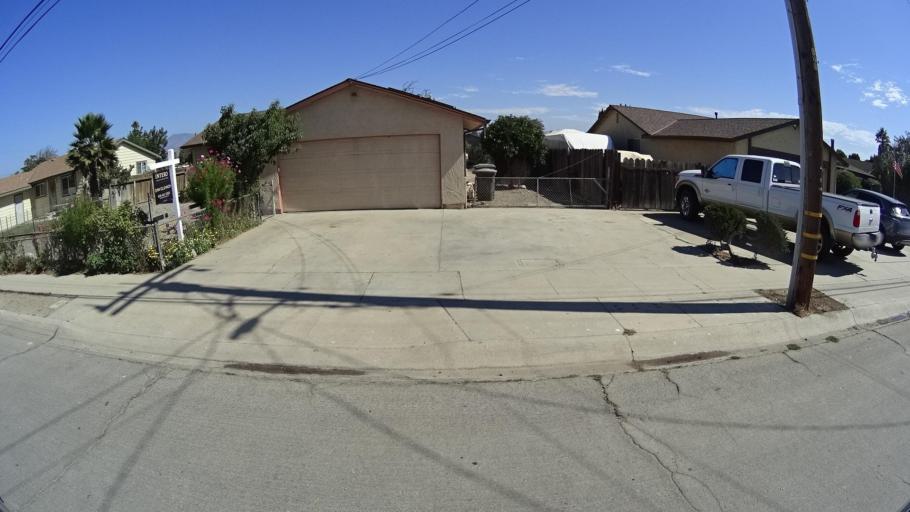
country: US
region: California
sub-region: Monterey County
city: Greenfield
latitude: 36.3248
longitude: -121.2353
